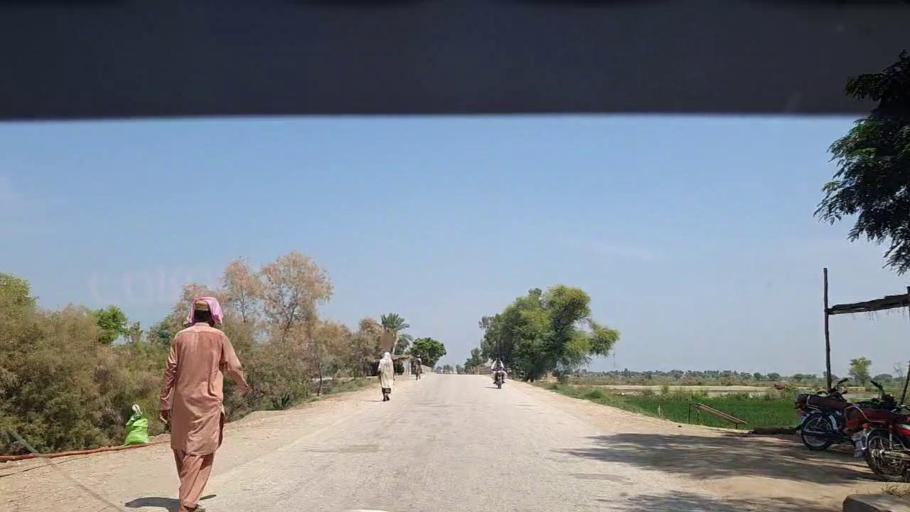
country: PK
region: Sindh
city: Thul
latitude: 28.1114
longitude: 68.8080
